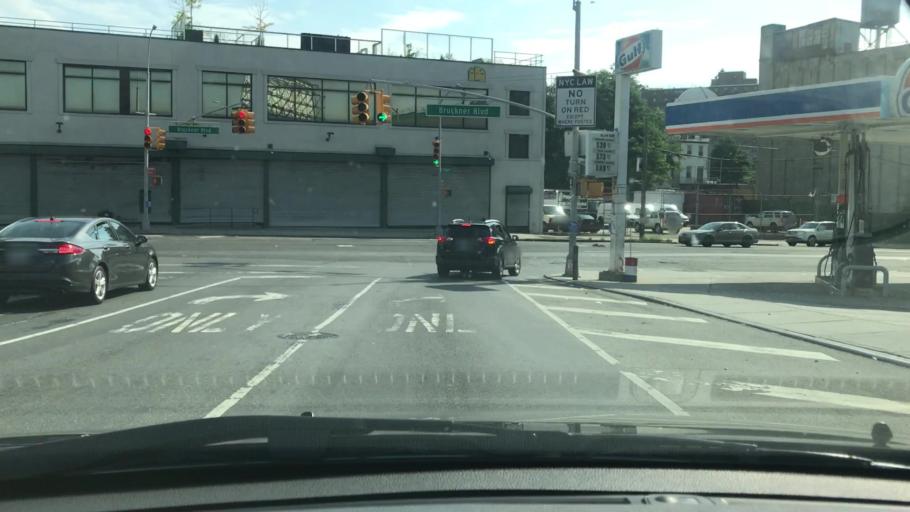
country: US
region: New York
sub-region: New York County
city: Manhattan
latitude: 40.8048
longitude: -73.9236
